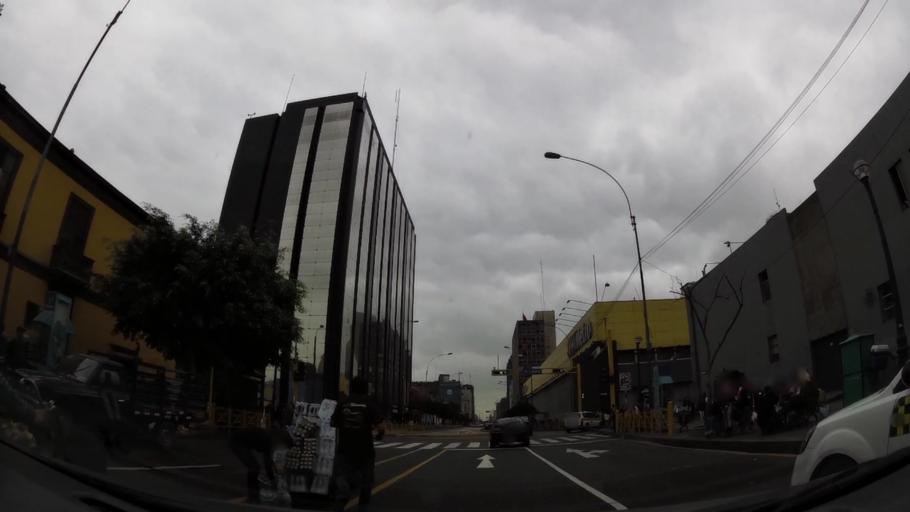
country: PE
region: Lima
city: Lima
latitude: -12.0503
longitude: -77.0311
